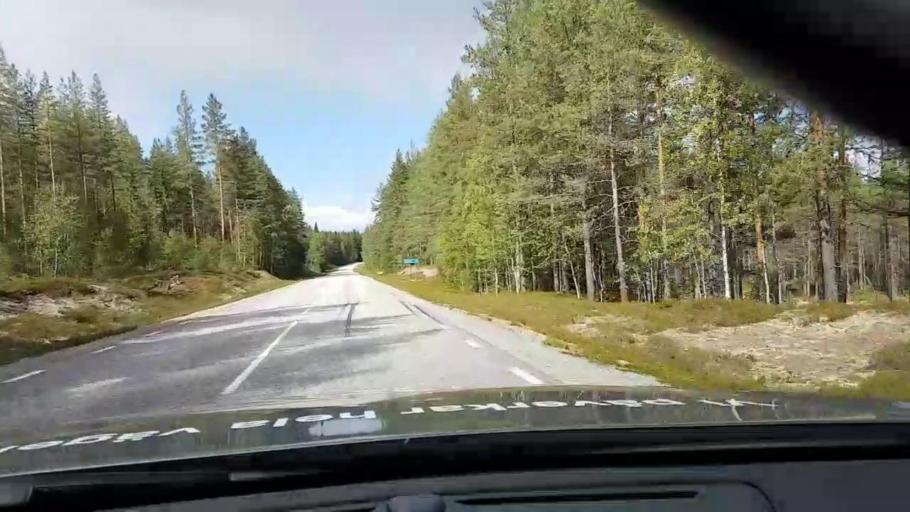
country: SE
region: Vaesternorrland
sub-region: OErnskoeldsviks Kommun
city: Bredbyn
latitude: 63.6914
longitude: 17.7693
